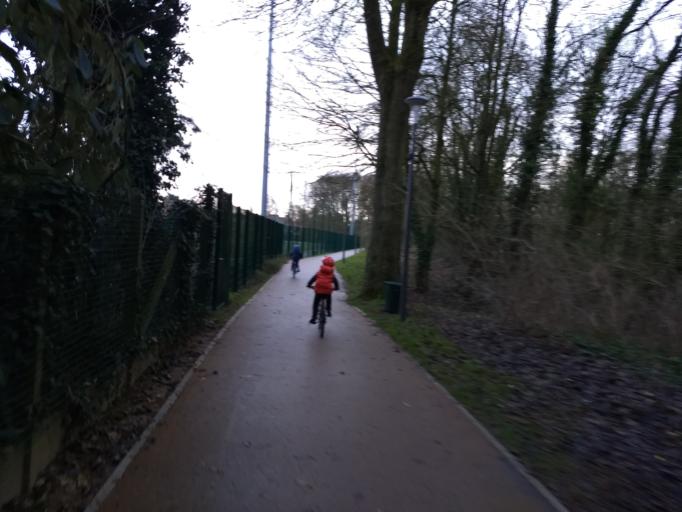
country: FR
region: Nord-Pas-de-Calais
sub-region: Departement du Pas-de-Calais
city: Achicourt
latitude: 50.2830
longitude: 2.7644
